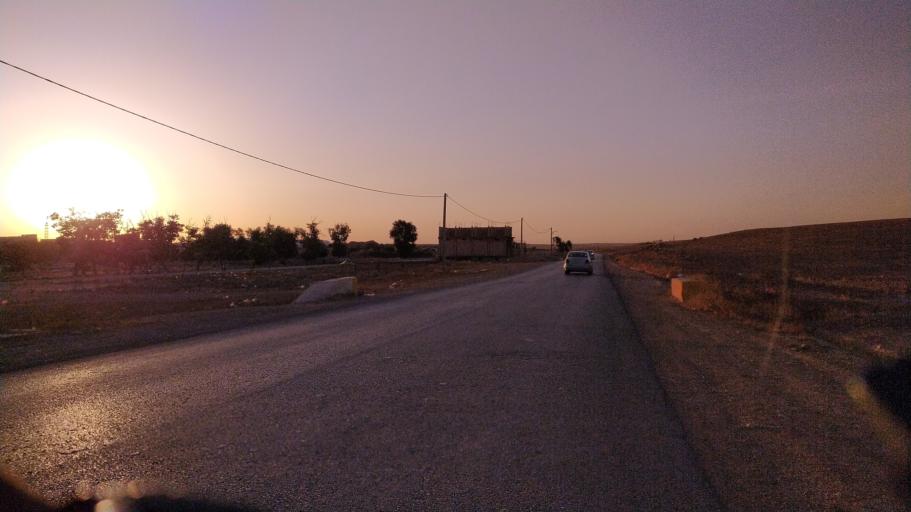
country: DZ
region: Tiaret
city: Frenda
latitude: 34.8997
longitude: 1.2449
